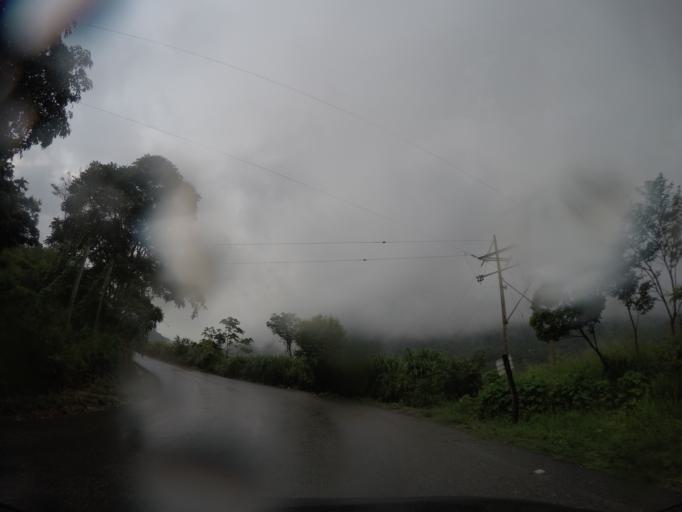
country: MX
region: Oaxaca
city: San Gabriel Mixtepec
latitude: 16.0746
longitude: -97.0834
